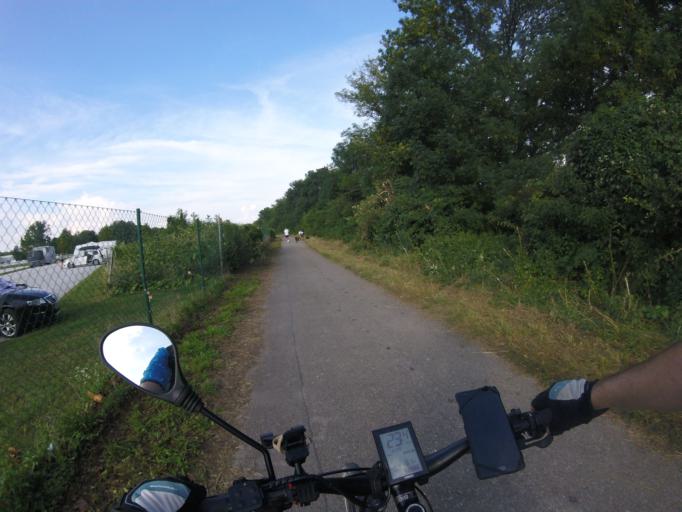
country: AT
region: Lower Austria
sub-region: Politischer Bezirk Baden
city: Ebreichsdorf
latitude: 47.9677
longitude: 16.3788
